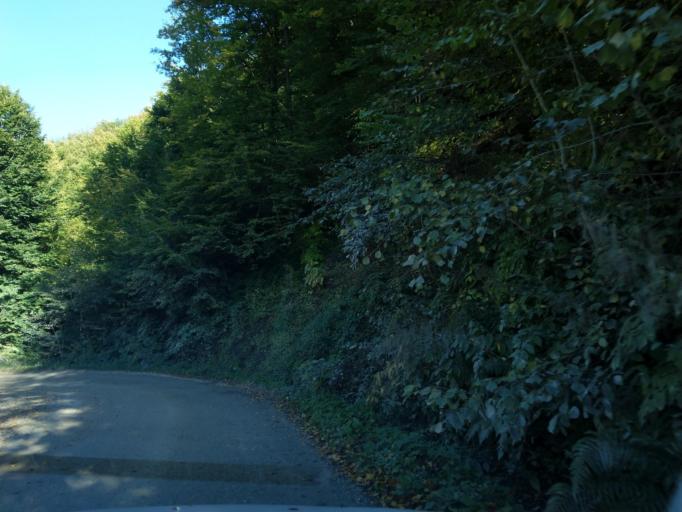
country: RS
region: Central Serbia
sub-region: Moravicki Okrug
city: Ivanjica
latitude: 43.4734
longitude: 20.2420
